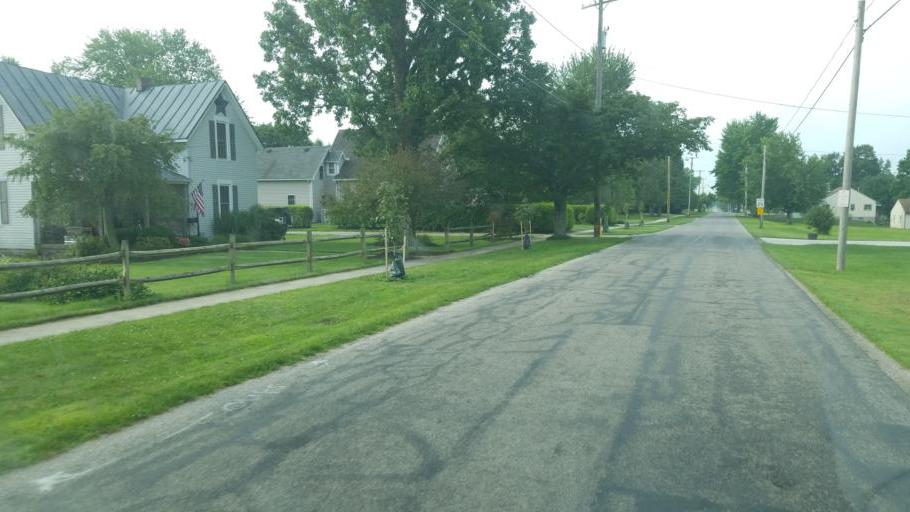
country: US
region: Ohio
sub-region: Morrow County
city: Cardington
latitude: 40.4929
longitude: -82.8941
